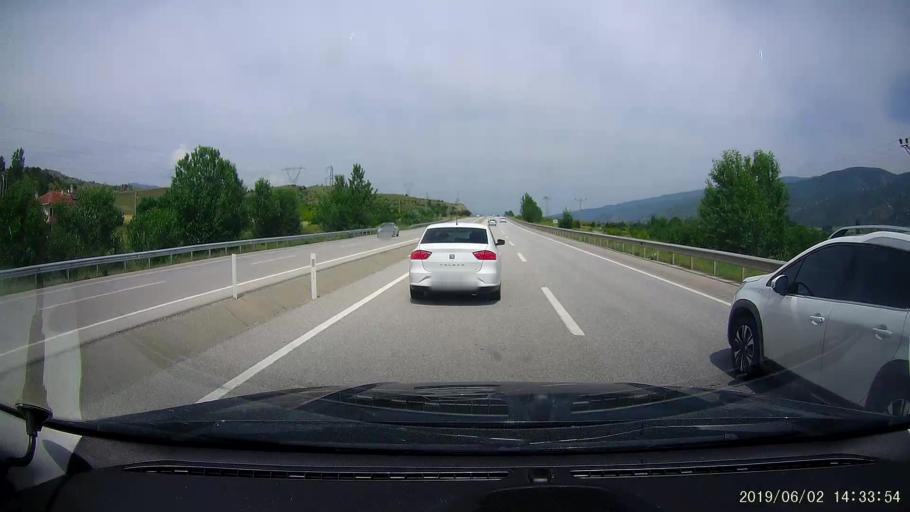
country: TR
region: Kastamonu
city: Tosya
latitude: 41.0343
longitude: 34.1809
